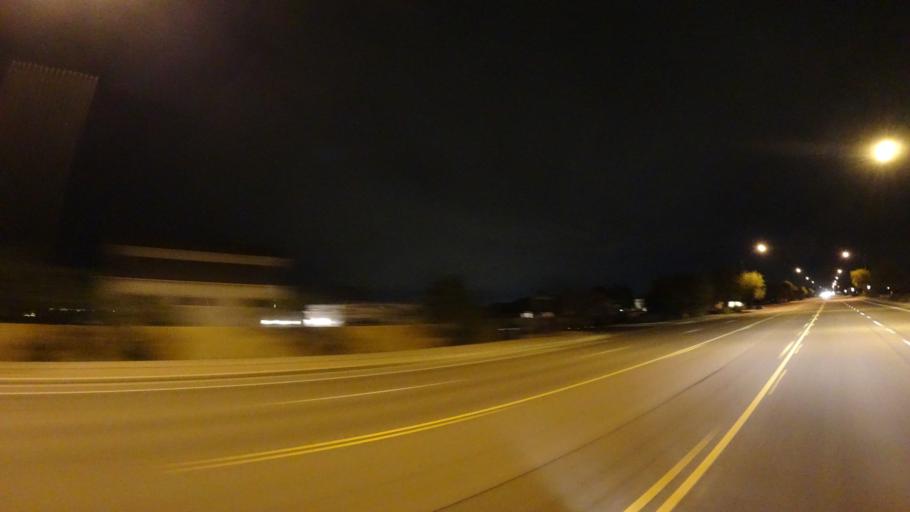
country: US
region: Arizona
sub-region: Maricopa County
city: Queen Creek
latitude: 33.2417
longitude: -111.7381
